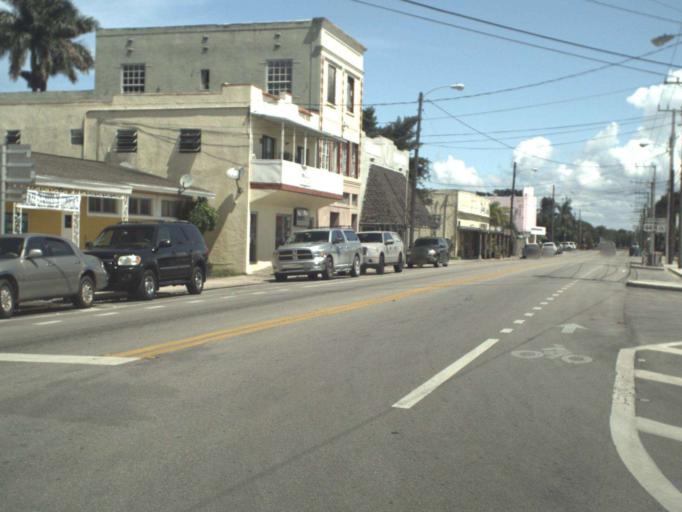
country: US
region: Florida
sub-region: Palm Beach County
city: Pahokee
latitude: 26.8241
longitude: -80.6657
